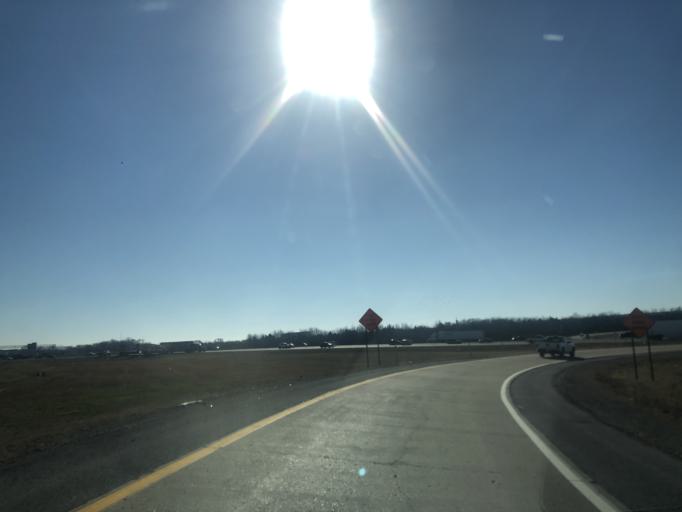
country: US
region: Tennessee
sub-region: Rutherford County
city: Murfreesboro
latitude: 35.8847
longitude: -86.4738
